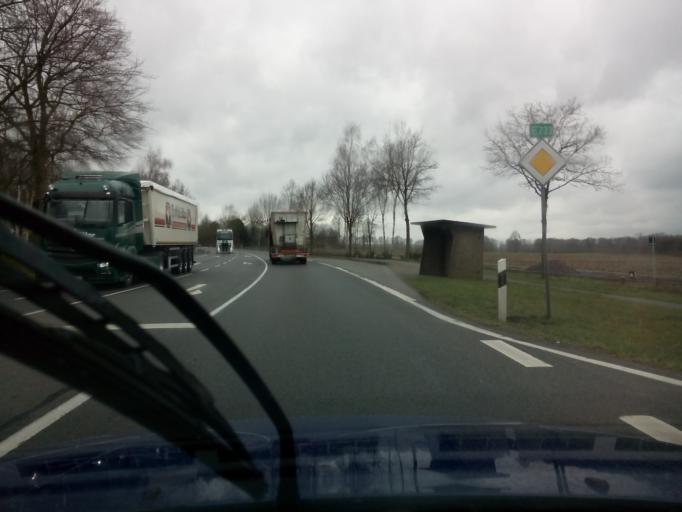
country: DE
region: Lower Saxony
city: Haselunne
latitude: 52.7017
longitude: 7.4210
